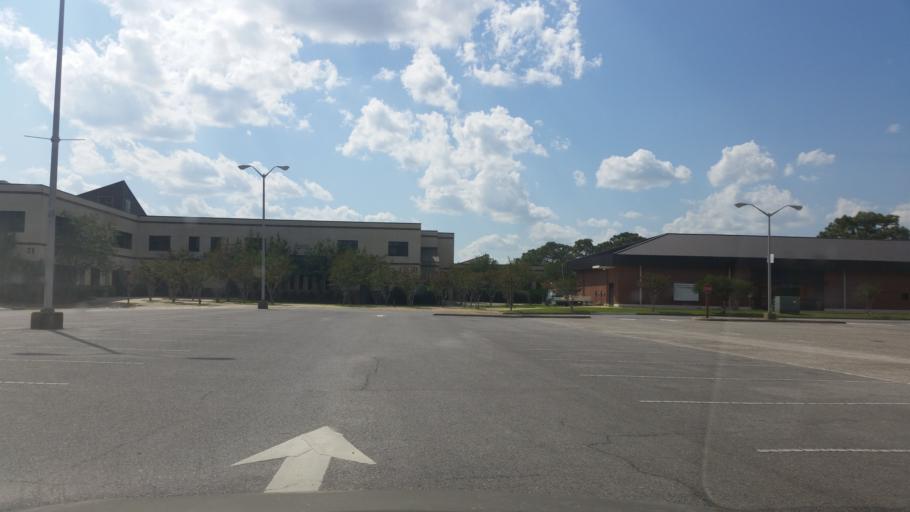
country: US
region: Florida
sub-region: Escambia County
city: Ferry Pass
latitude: 30.4780
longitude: -87.2037
